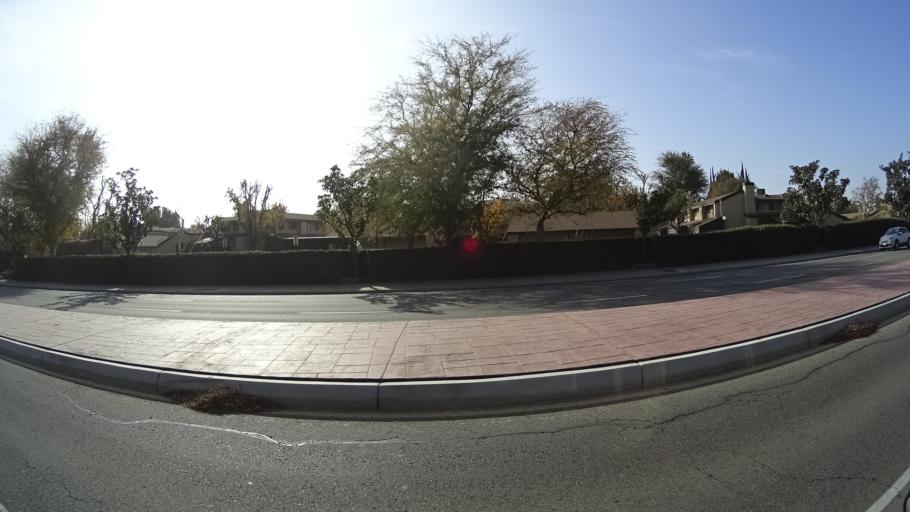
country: US
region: California
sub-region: Kern County
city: Bakersfield
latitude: 35.3633
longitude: -119.0642
